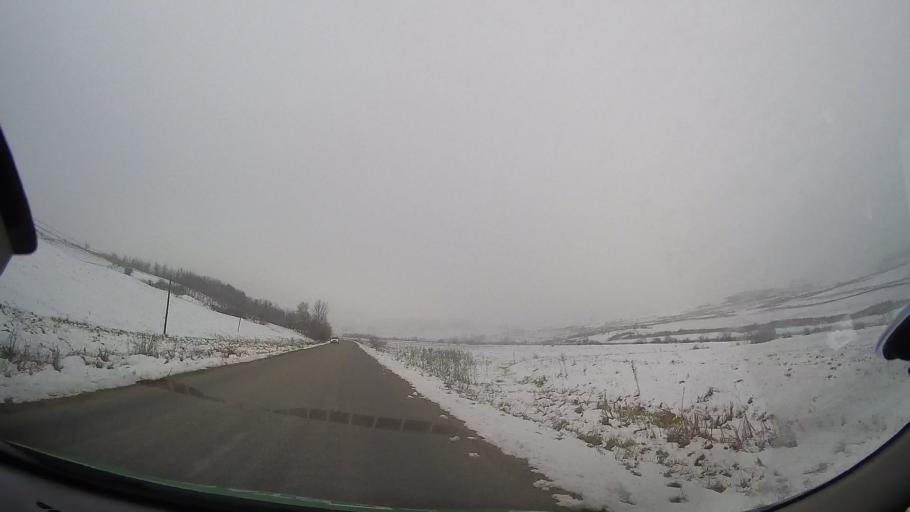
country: RO
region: Bacau
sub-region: Comuna Vultureni
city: Vultureni
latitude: 46.3131
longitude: 27.2929
